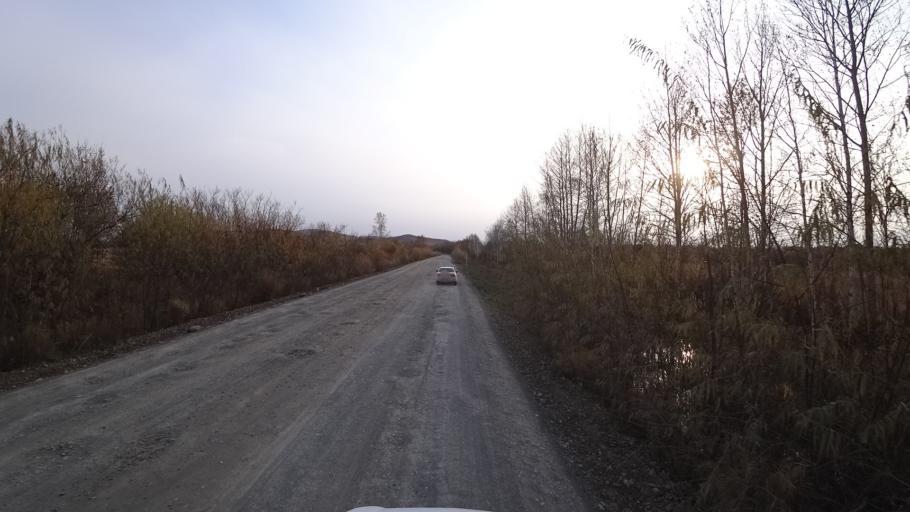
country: RU
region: Khabarovsk Krai
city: Amursk
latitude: 50.0707
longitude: 136.4874
